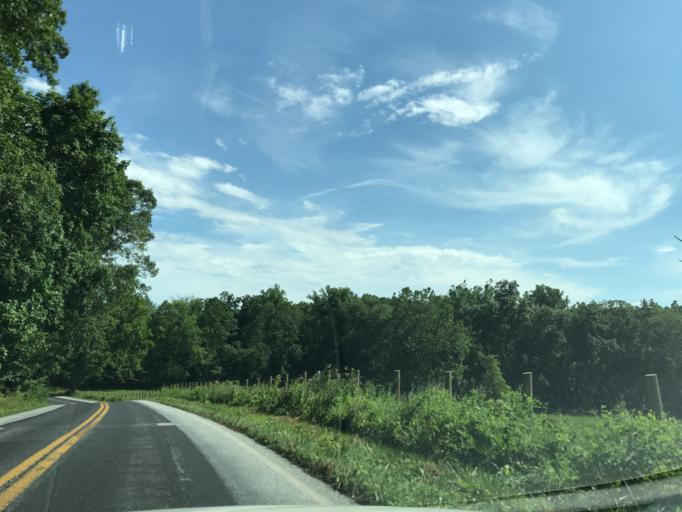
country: US
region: Pennsylvania
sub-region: York County
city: Pennville
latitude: 39.7682
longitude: -77.0065
